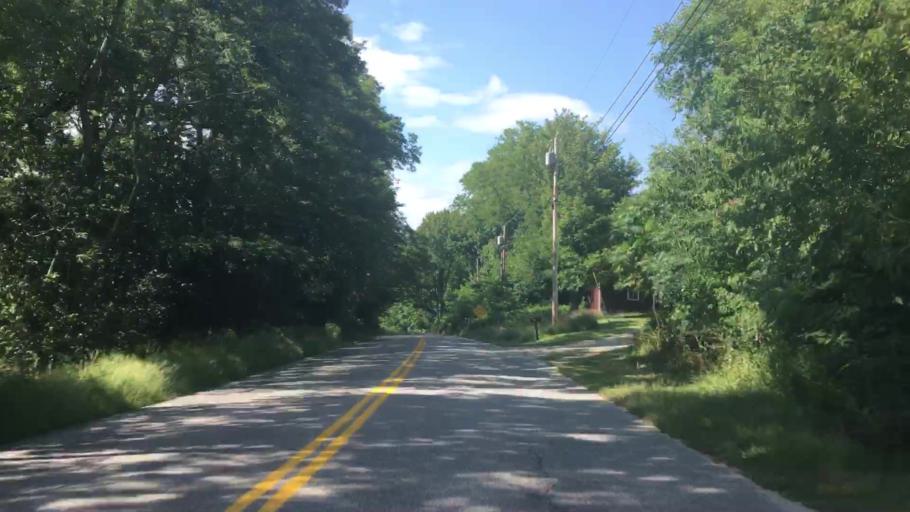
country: US
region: Maine
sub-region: Androscoggin County
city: Poland
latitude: 44.0070
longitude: -70.3746
